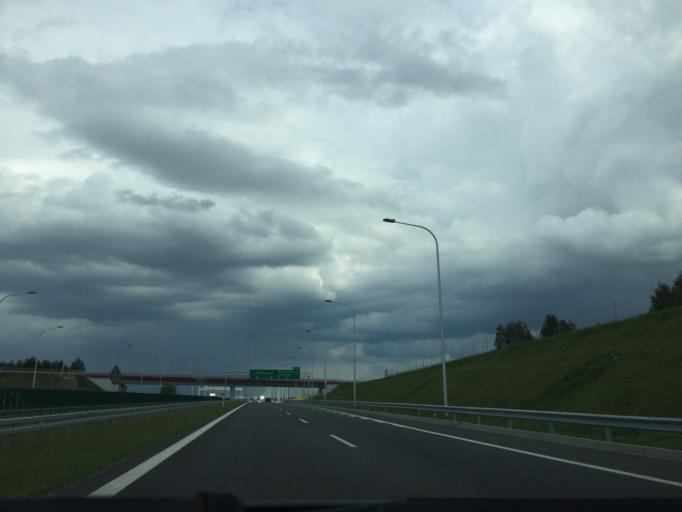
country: PL
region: Masovian Voivodeship
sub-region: Powiat szydlowiecki
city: Jastrzab
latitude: 51.2557
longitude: 20.9120
